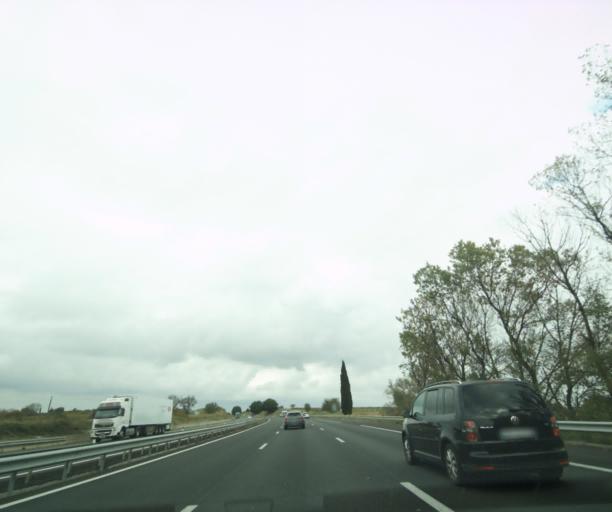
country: FR
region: Languedoc-Roussillon
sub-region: Departement de l'Herault
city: Meze
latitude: 43.4286
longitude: 3.5600
